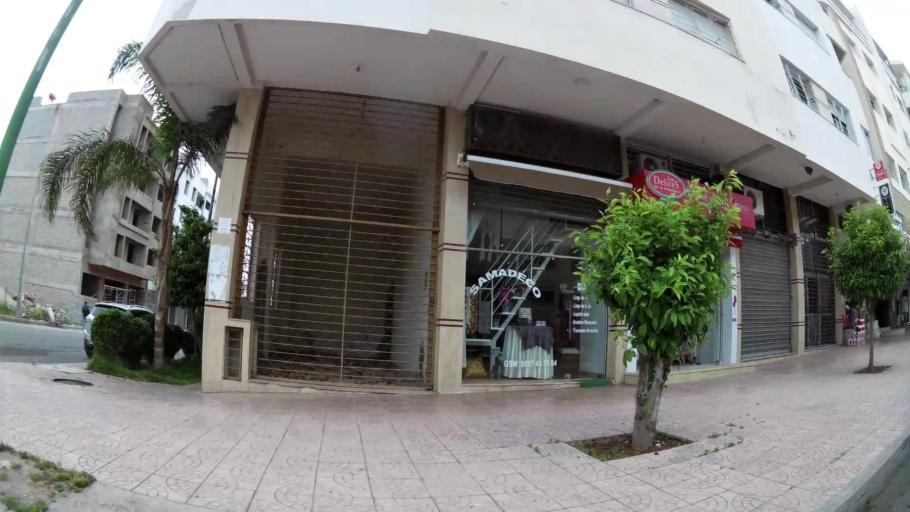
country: MA
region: Fes-Boulemane
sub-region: Fes
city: Fes
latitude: 34.0379
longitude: -5.0164
